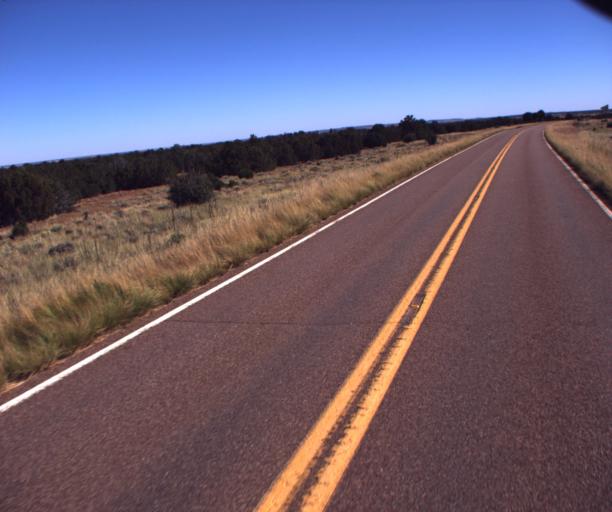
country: US
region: Arizona
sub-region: Navajo County
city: Heber-Overgaard
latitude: 34.4589
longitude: -110.4357
